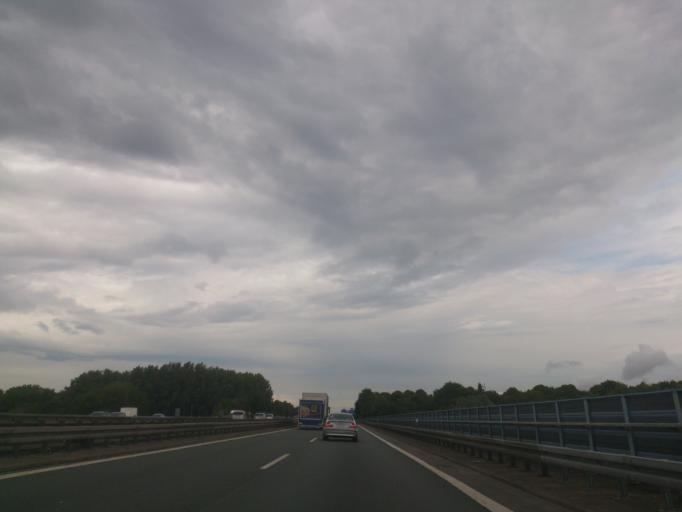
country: DE
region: North Rhine-Westphalia
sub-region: Regierungsbezirk Arnsberg
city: Holzwickede
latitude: 51.5141
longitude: 7.6546
